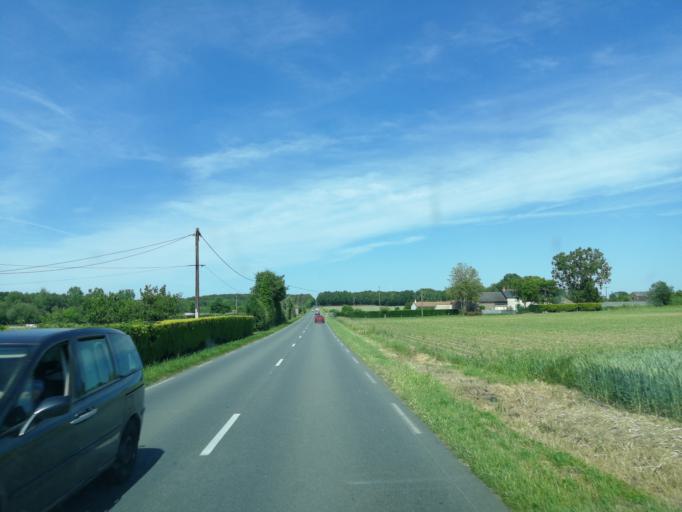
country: FR
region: Poitou-Charentes
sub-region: Departement des Deux-Sevres
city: Saint-Varent
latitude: 46.9271
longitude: -0.2563
